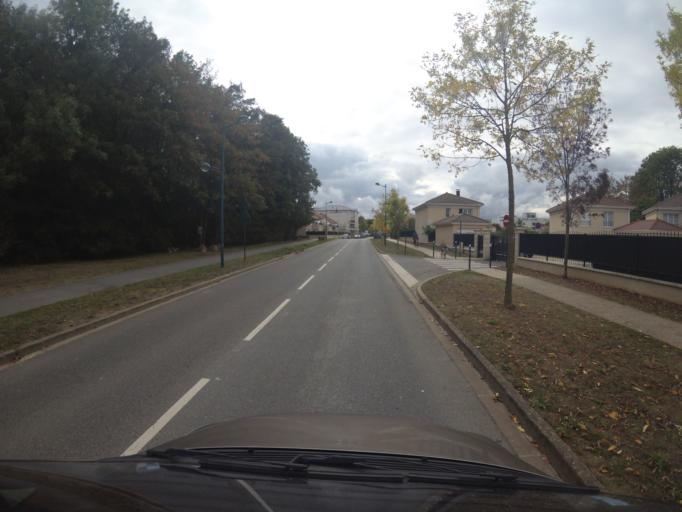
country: FR
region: Ile-de-France
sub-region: Departement de Seine-et-Marne
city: Montevrain
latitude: 48.8683
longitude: 2.7616
